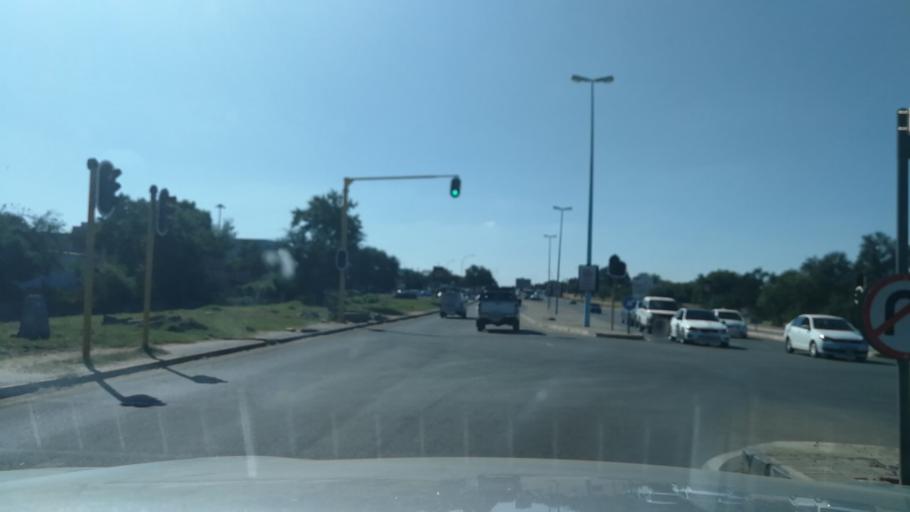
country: BW
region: South East
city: Gaborone
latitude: -24.6813
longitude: 25.9060
